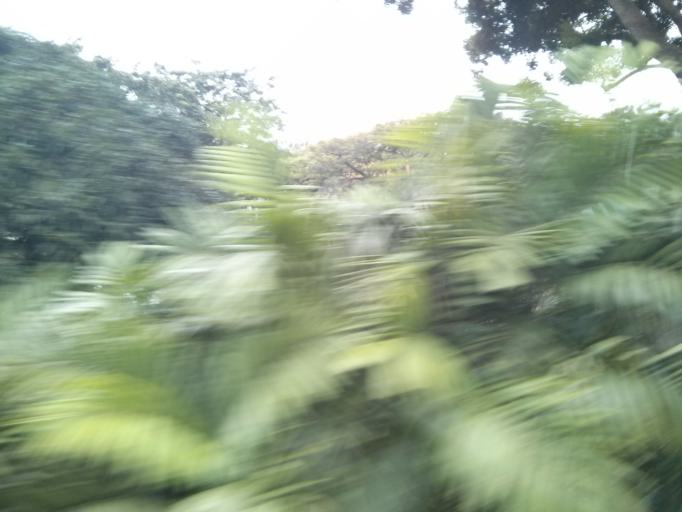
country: SG
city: Singapore
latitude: 1.2849
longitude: 103.8008
